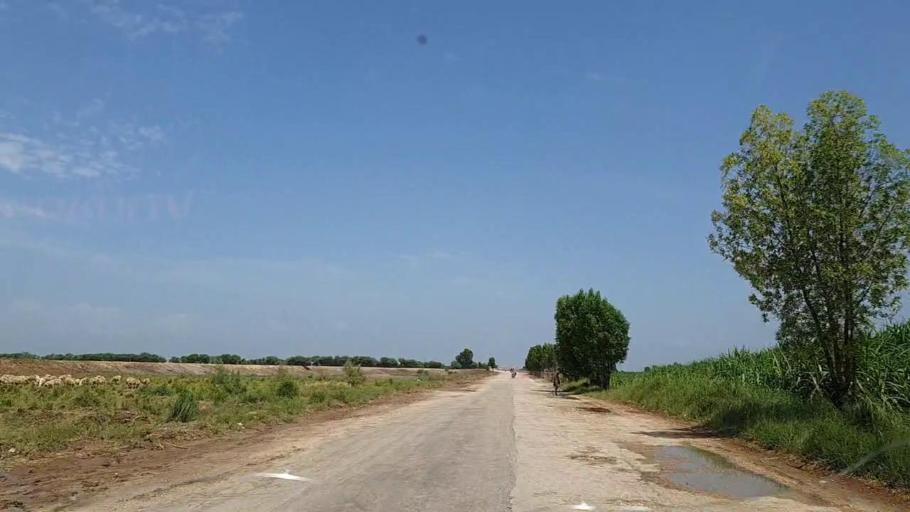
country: PK
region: Sindh
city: Naushahro Firoz
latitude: 26.8260
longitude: 68.1530
